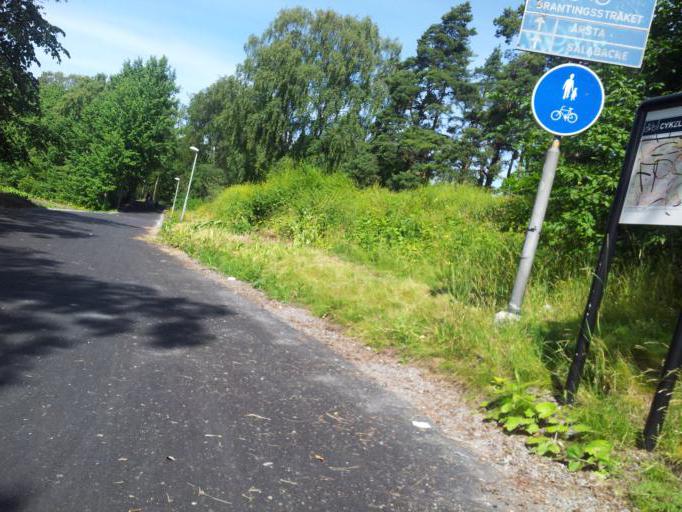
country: SE
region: Uppsala
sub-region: Uppsala Kommun
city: Uppsala
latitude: 59.8542
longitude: 17.6736
